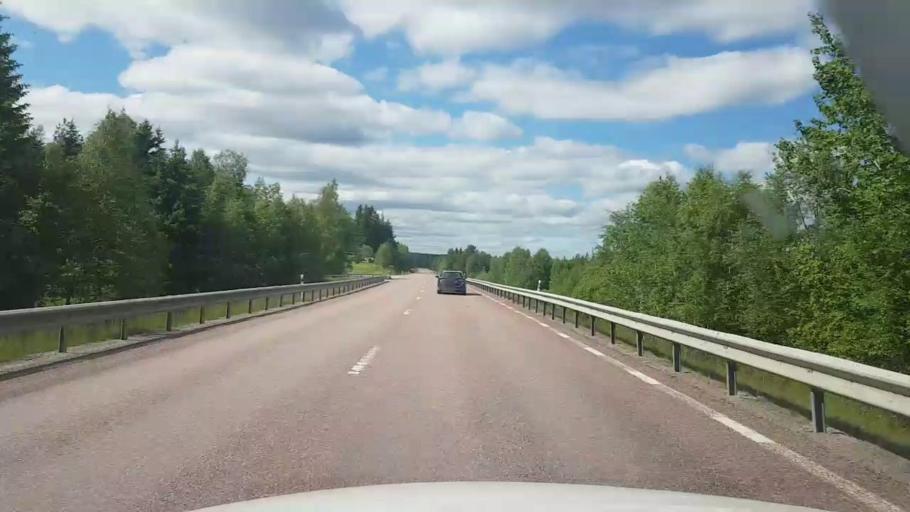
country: SE
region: Gaevleborg
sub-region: Ljusdals Kommun
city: Jaervsoe
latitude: 61.7732
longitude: 16.1523
